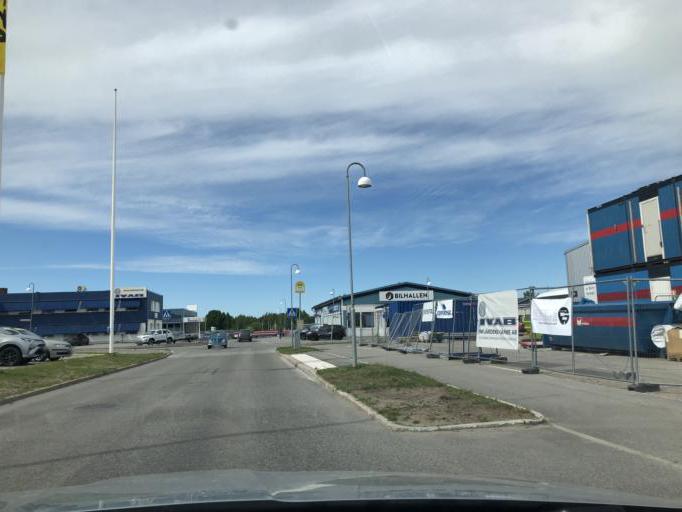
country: SE
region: Norrbotten
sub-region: Pitea Kommun
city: Pitea
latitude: 65.3226
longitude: 21.4440
